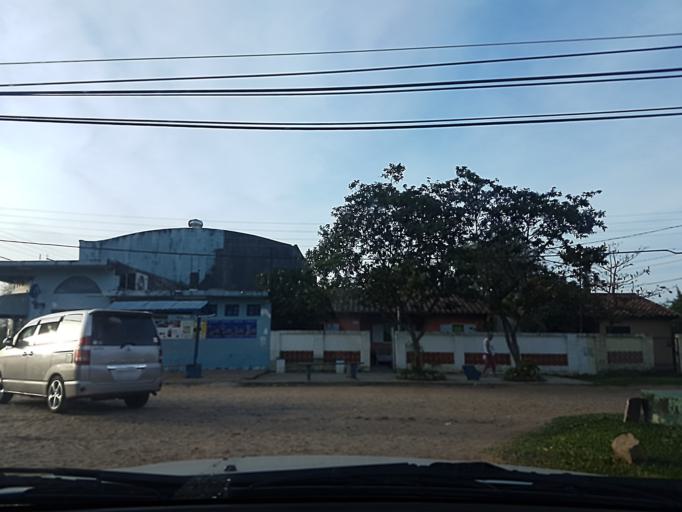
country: PY
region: Central
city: Colonia Mariano Roque Alonso
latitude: -25.2031
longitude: -57.5417
